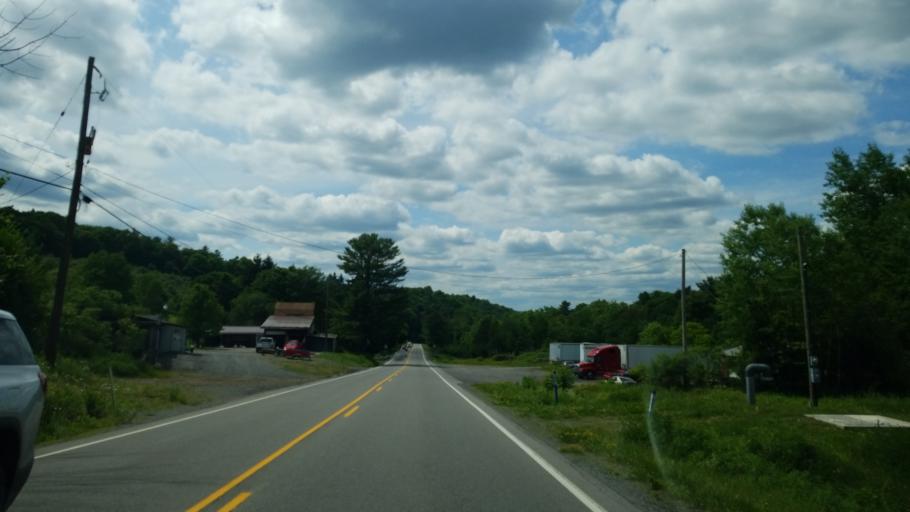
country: US
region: Pennsylvania
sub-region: Clearfield County
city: Clearfield
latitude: 40.9737
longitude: -78.3812
